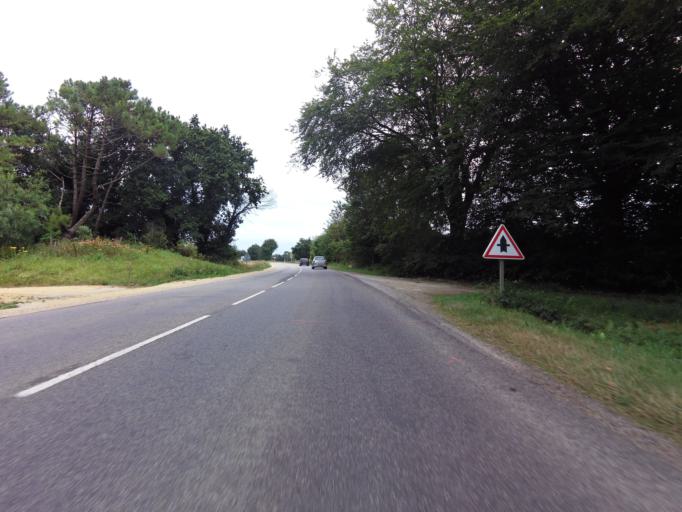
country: FR
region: Brittany
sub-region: Departement du Finistere
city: Douarnenez
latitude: 48.0807
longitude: -4.3600
